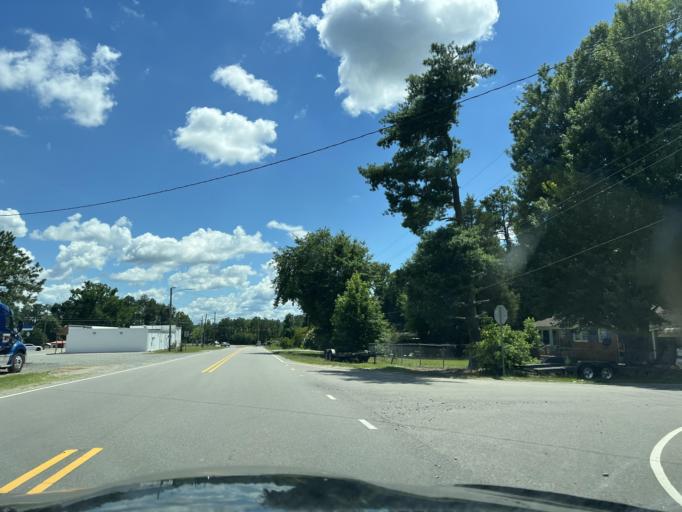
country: US
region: North Carolina
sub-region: Lee County
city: Sanford
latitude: 35.4469
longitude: -79.1721
